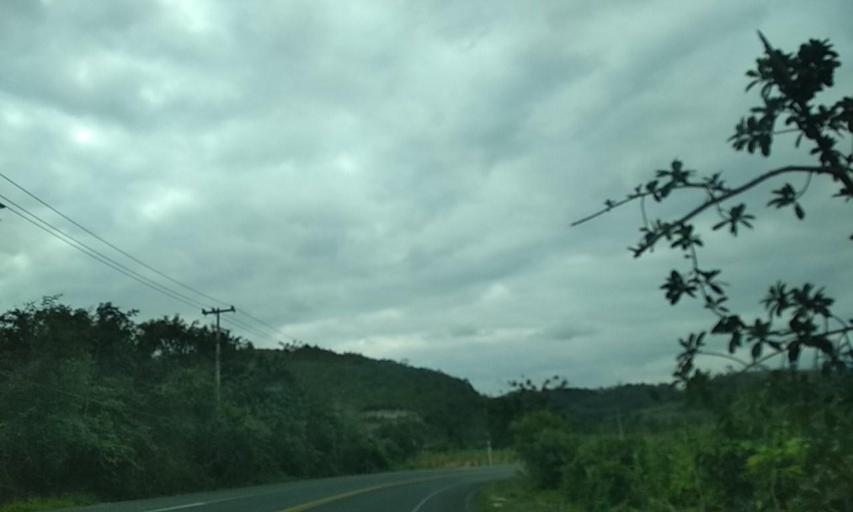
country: MX
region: Veracruz
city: Papantla de Olarte
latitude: 20.4683
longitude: -97.3210
